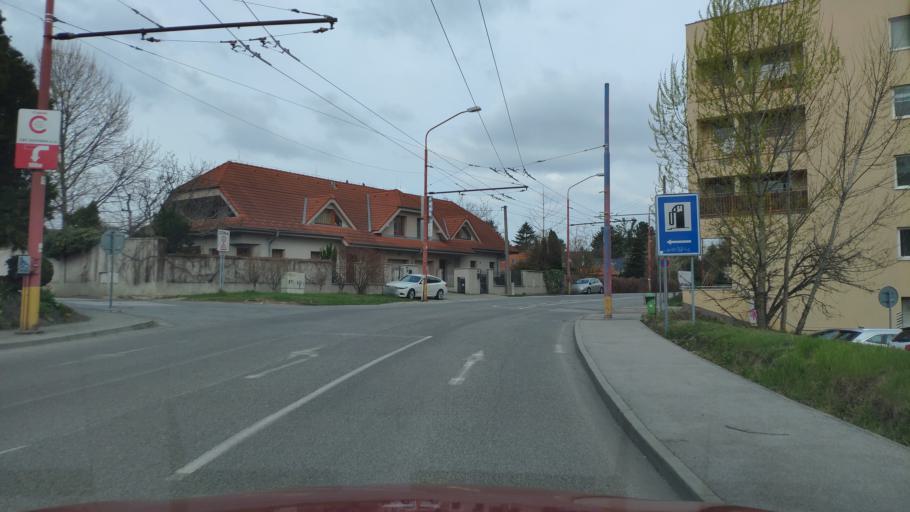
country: SK
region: Bratislavsky
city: Bratislava
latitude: 48.1446
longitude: 17.1867
